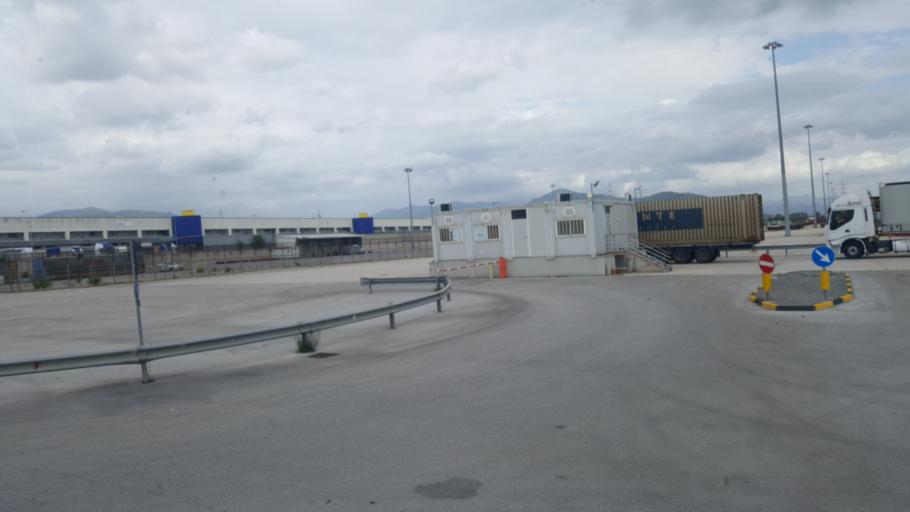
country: IT
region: Campania
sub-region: Provincia di Caserta
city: Maddaloni
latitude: 41.0093
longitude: 14.3675
